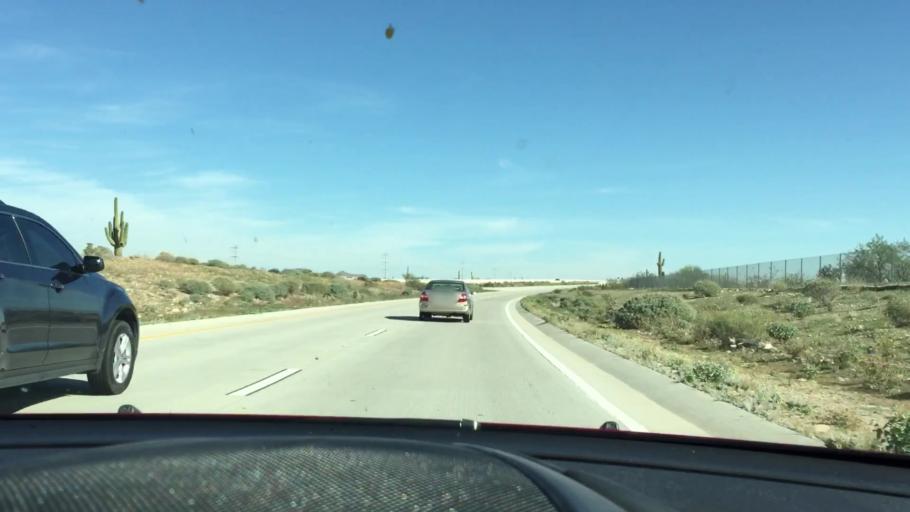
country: US
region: Arizona
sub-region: Maricopa County
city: Anthem
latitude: 33.7814
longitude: -112.1997
